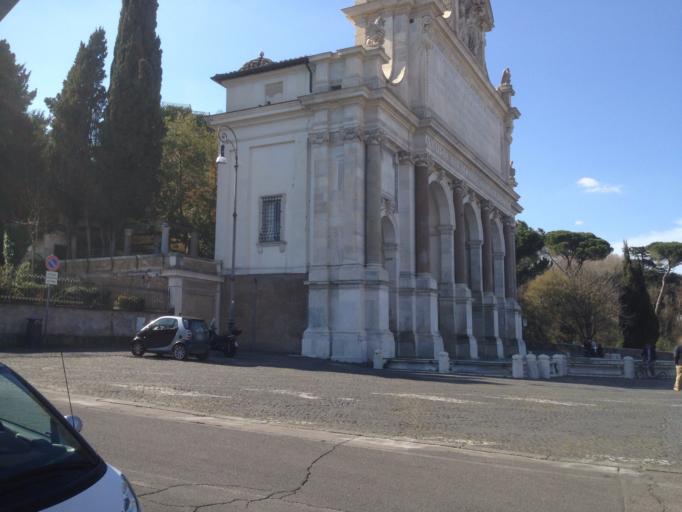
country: VA
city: Vatican City
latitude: 41.8886
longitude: 12.4646
